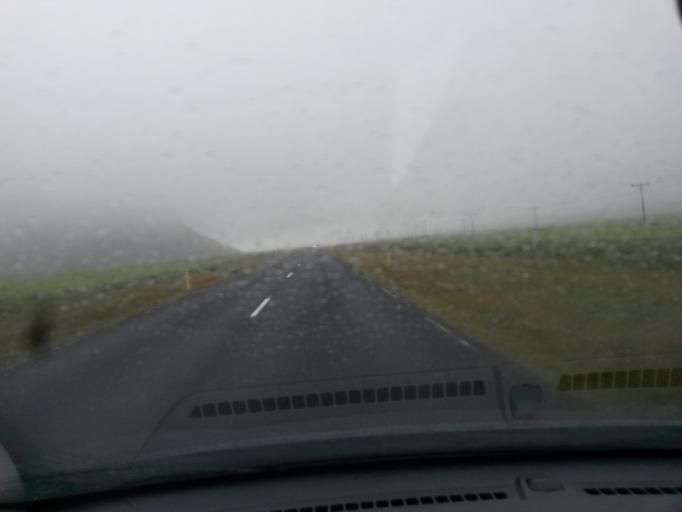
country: IS
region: South
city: Vestmannaeyjar
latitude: 63.4665
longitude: -19.2419
